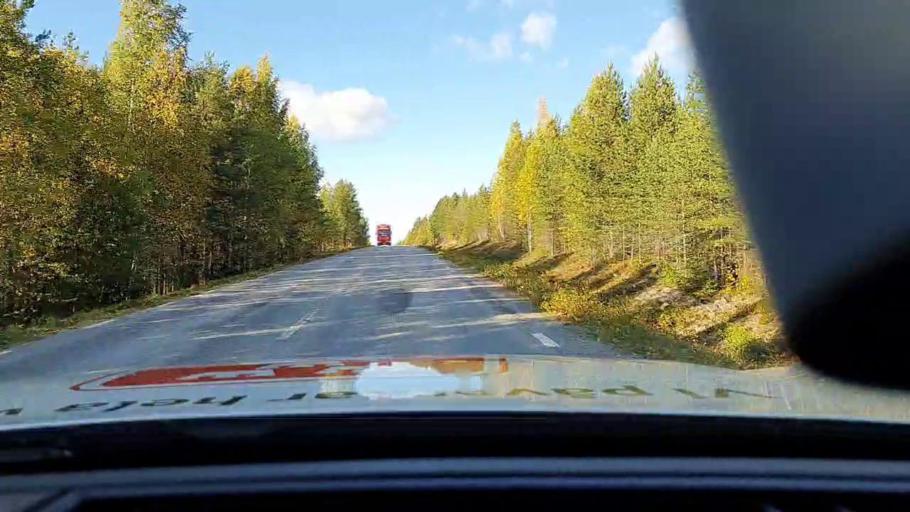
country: SE
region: Norrbotten
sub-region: Pitea Kommun
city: Norrfjarden
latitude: 65.4518
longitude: 21.4567
